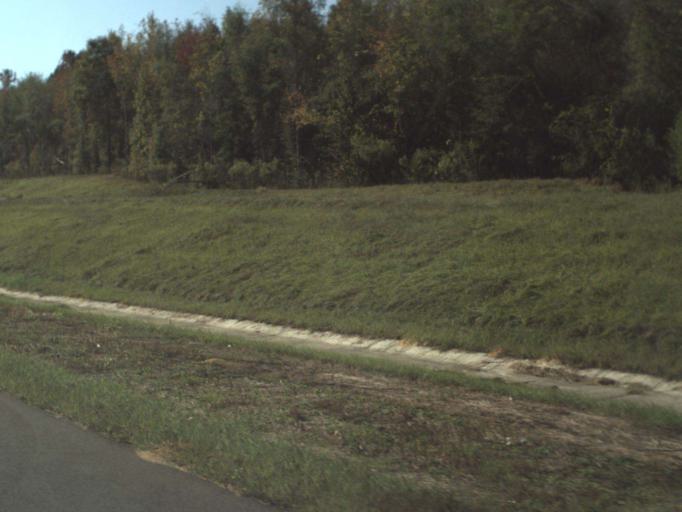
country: US
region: Florida
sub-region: Gadsden County
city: Quincy
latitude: 30.5768
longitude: -84.5482
